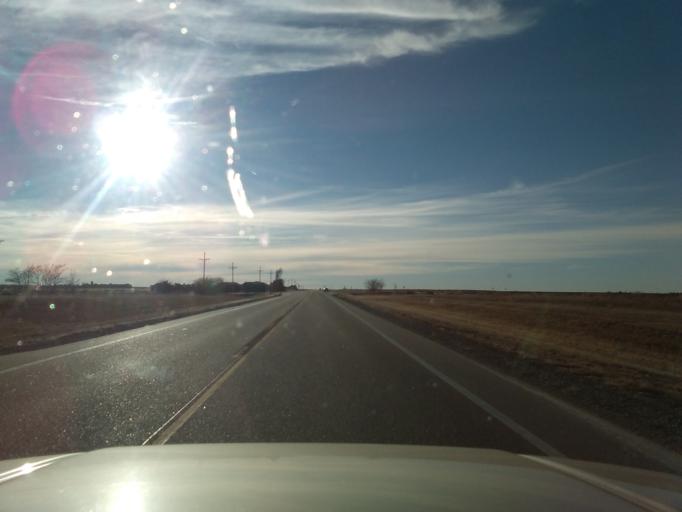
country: US
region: Kansas
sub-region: Sheridan County
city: Hoxie
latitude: 39.5397
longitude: -100.5781
